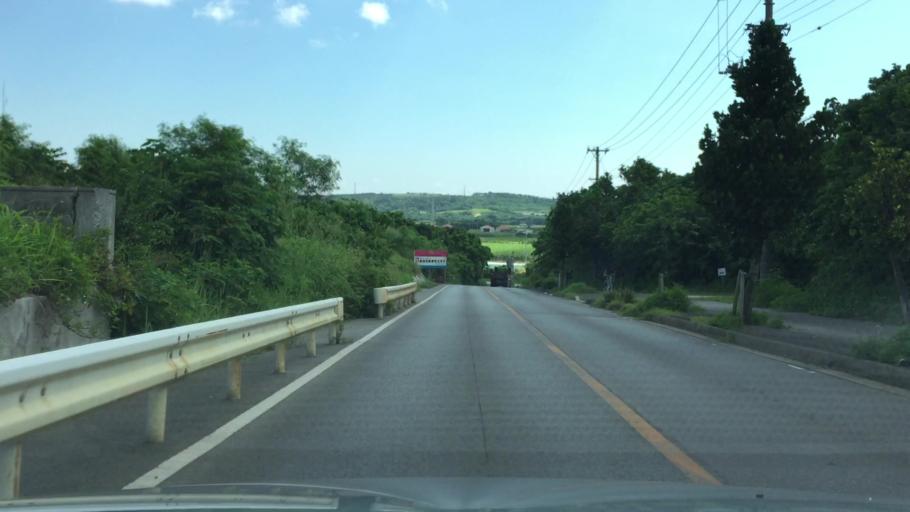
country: JP
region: Okinawa
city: Ishigaki
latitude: 24.3547
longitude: 124.1920
